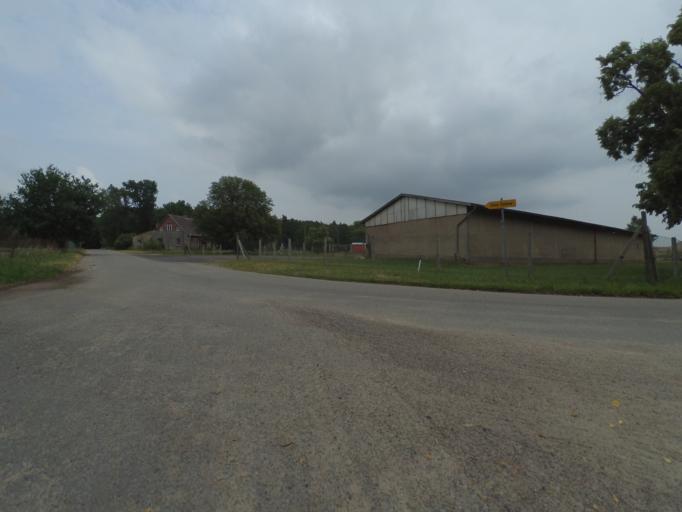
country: DE
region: Mecklenburg-Vorpommern
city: Siggelkow
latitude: 53.3626
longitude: 12.0247
